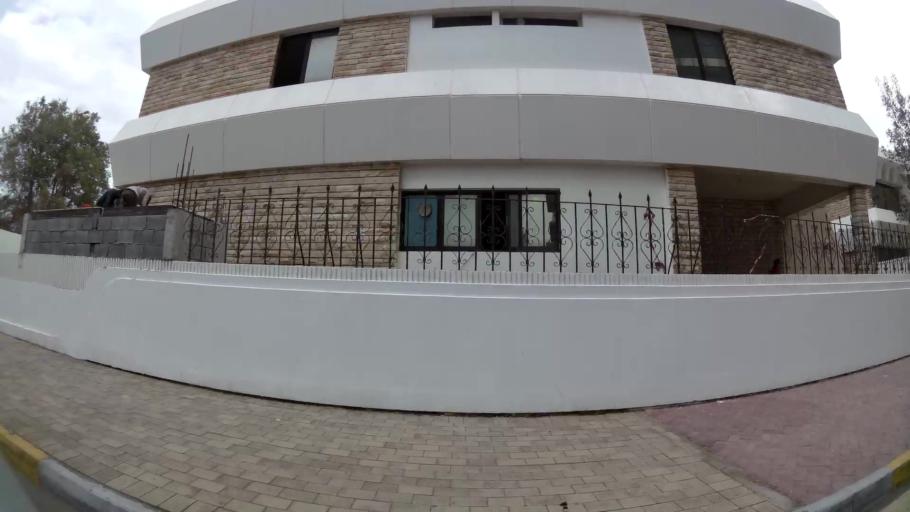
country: AE
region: Abu Dhabi
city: Abu Dhabi
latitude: 24.4679
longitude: 54.3347
